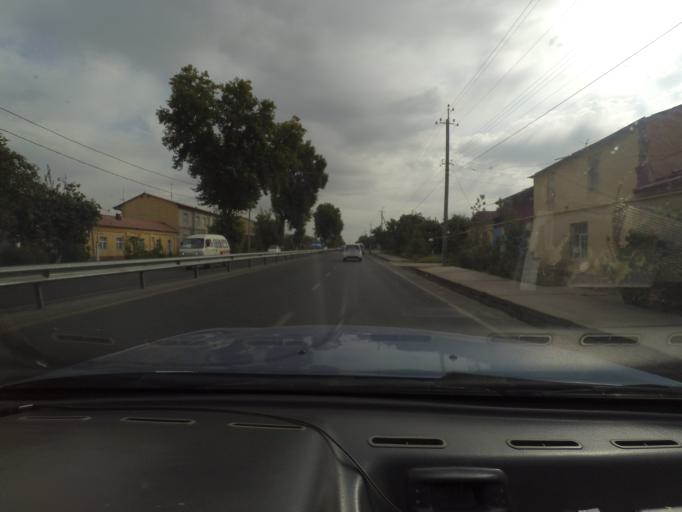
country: UZ
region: Toshkent
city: Qibray
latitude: 41.4012
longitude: 69.4917
